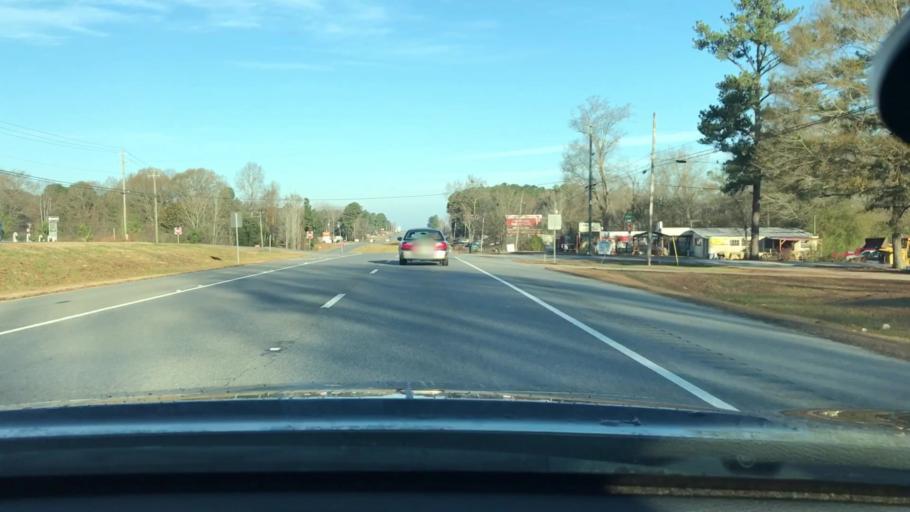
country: US
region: Alabama
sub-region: Talladega County
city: Childersburg
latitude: 33.2472
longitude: -86.3381
